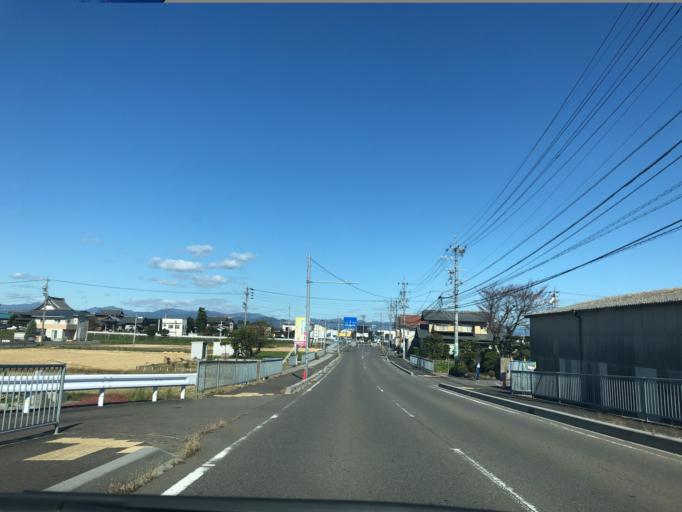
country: JP
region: Gifu
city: Ogaki
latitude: 35.3775
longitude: 136.6687
